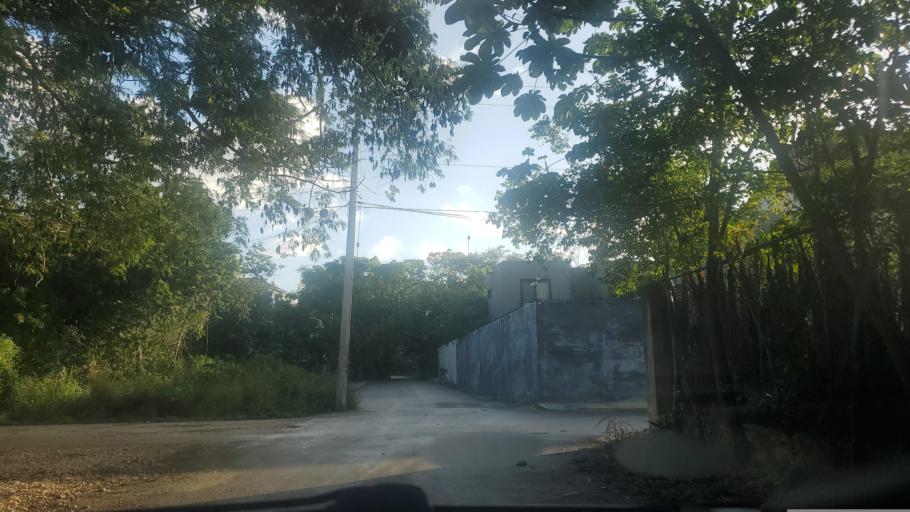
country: MX
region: Quintana Roo
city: Tulum
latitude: 20.2093
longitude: -87.4754
